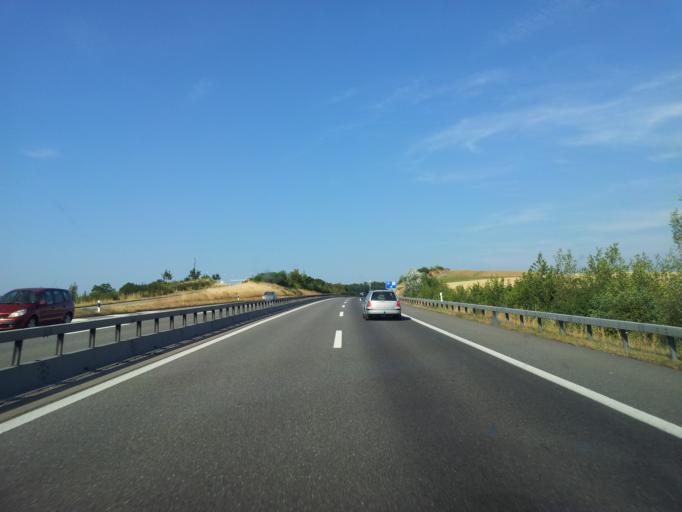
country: CH
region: Fribourg
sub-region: Sense District
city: Bosingen
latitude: 46.8682
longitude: 7.2176
